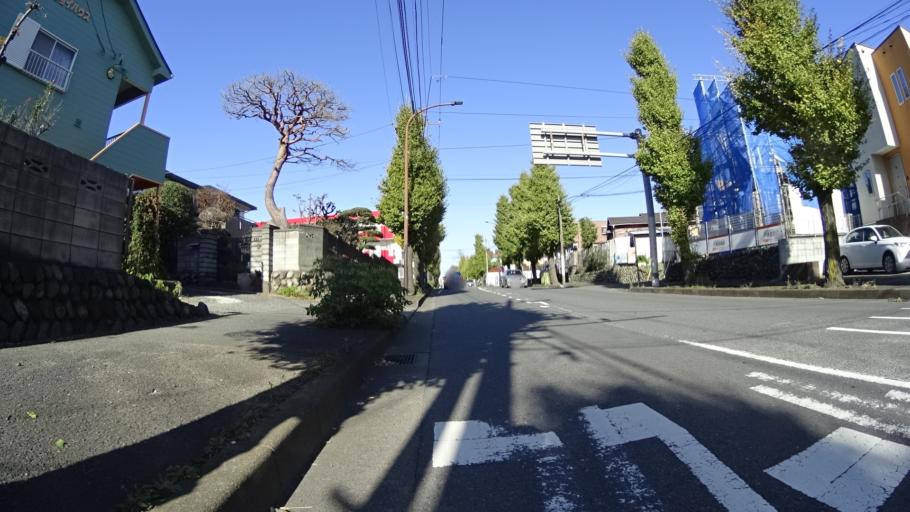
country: JP
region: Tokyo
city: Hachioji
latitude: 35.5752
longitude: 139.3601
